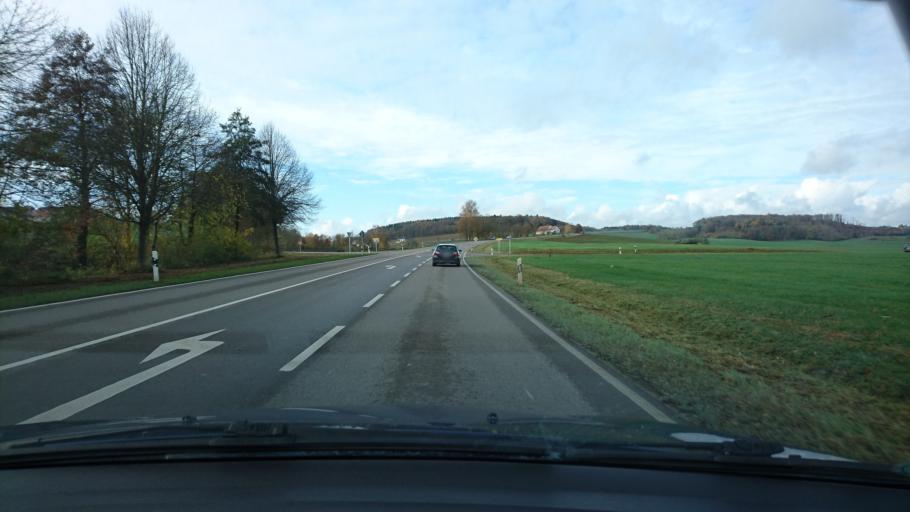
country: DE
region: Bavaria
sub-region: Swabia
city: Bissingen
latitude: 48.7187
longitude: 10.6060
